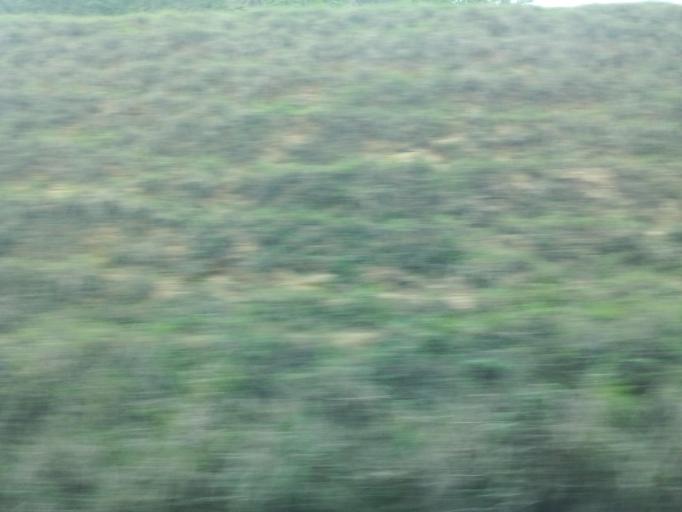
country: BR
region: Minas Gerais
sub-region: Belo Oriente
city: Belo Oriente
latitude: -19.2260
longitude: -42.3003
